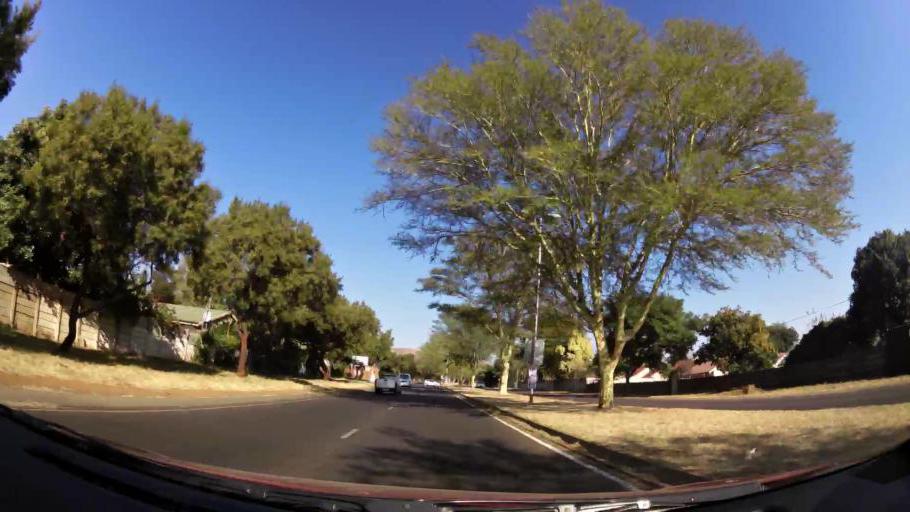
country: ZA
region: Gauteng
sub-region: City of Tshwane Metropolitan Municipality
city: Pretoria
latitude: -25.6781
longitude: 28.1617
